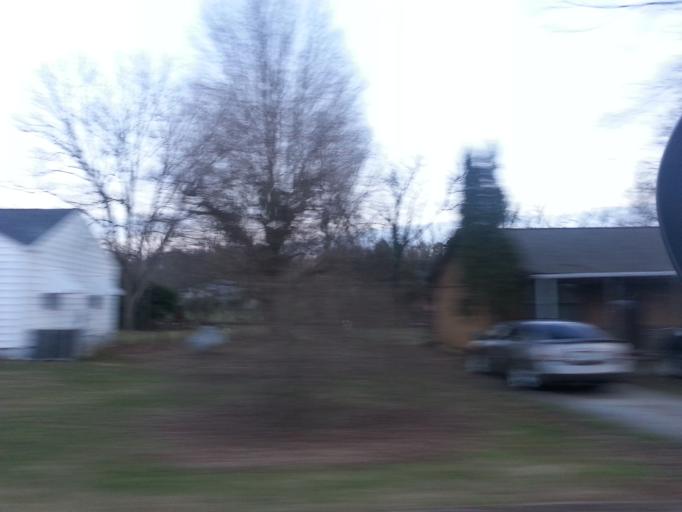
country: US
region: Tennessee
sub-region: Knox County
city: Knoxville
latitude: 35.9390
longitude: -83.9034
